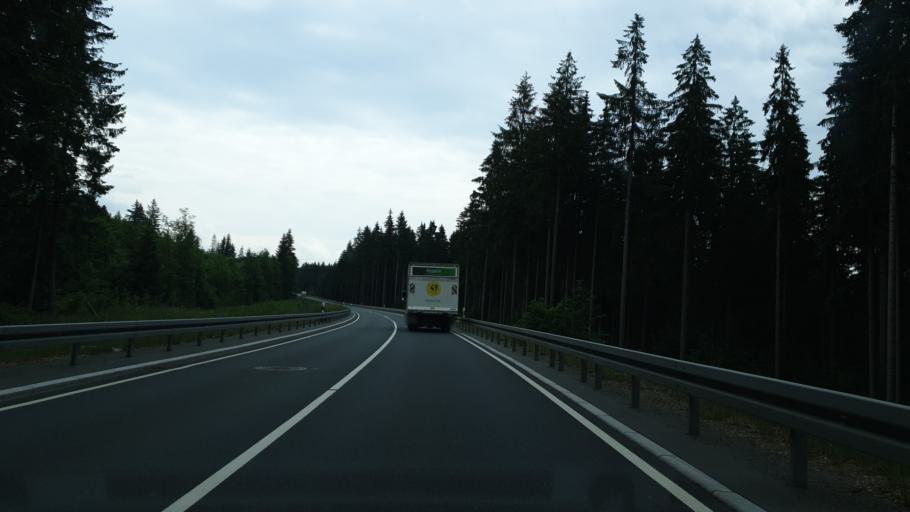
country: DE
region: Saxony
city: Hammerbrucke
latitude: 50.4689
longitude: 12.4333
